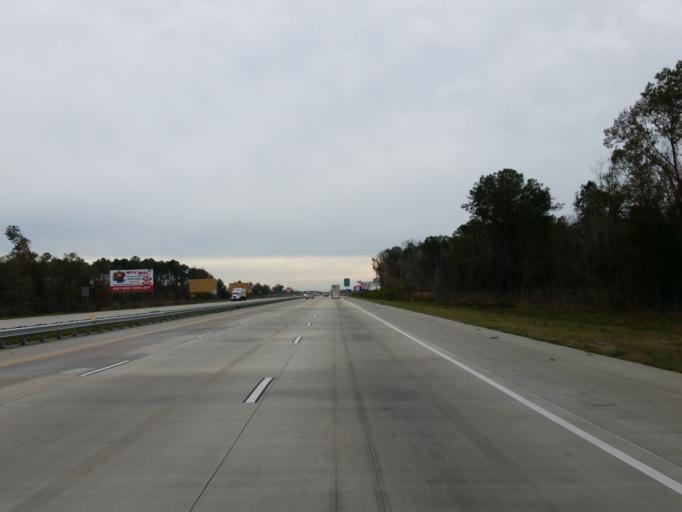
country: US
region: Georgia
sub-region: Dooly County
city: Vienna
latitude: 32.1002
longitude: -83.7632
